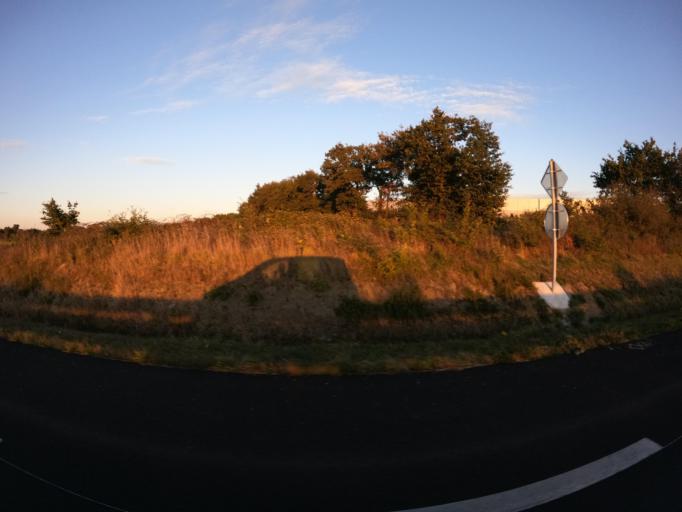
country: FR
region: Pays de la Loire
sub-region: Departement de la Vendee
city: Saint-Andre-Treize-Voies
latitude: 46.9017
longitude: -1.3848
